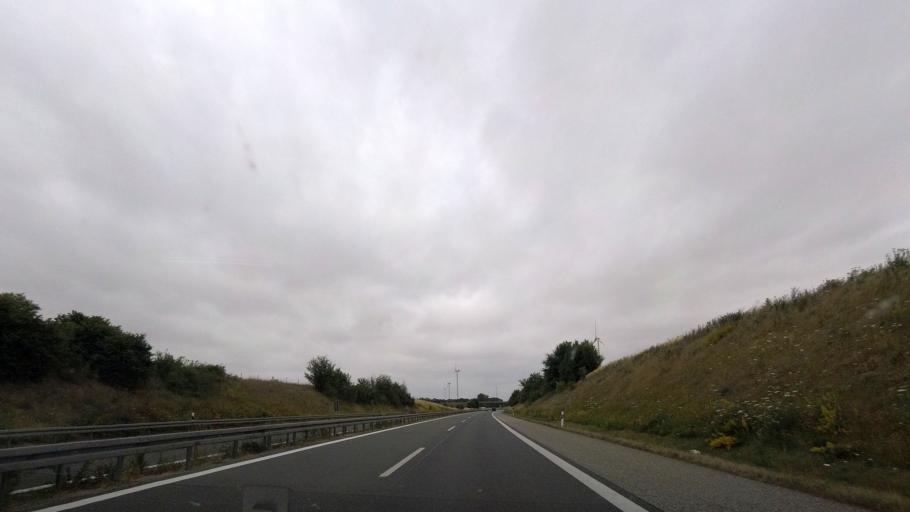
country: DE
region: Brandenburg
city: Schenkenberg
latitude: 53.3592
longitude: 13.9749
